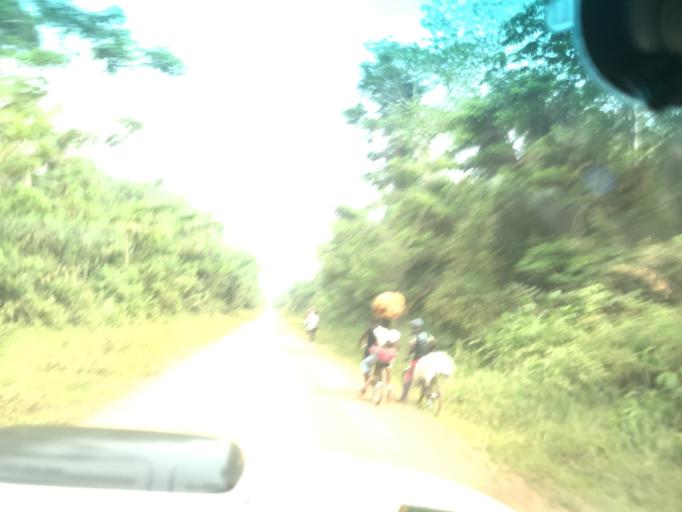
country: CD
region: Eastern Province
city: Buta
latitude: 2.8719
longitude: 24.4882
